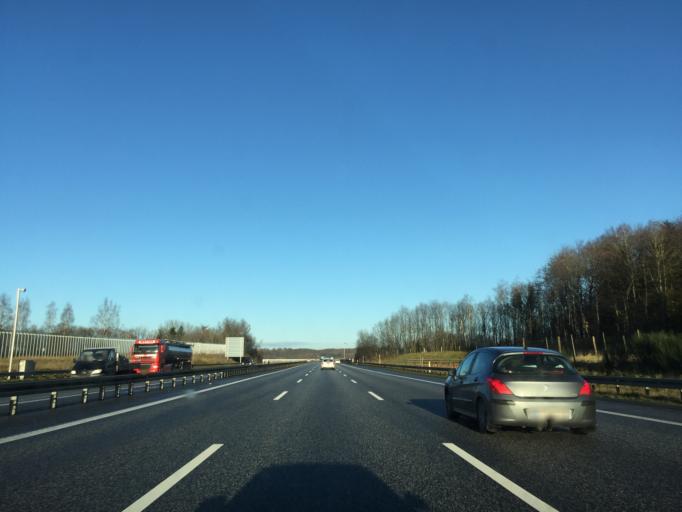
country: DK
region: South Denmark
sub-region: Vejle Kommune
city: Vejle
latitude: 55.6901
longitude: 9.5690
